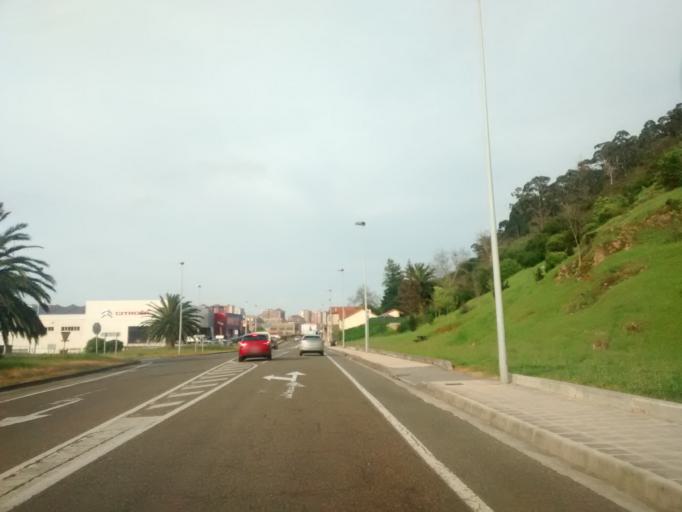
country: ES
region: Cantabria
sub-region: Provincia de Cantabria
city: Santa Cruz de Bezana
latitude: 43.4505
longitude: -3.8601
